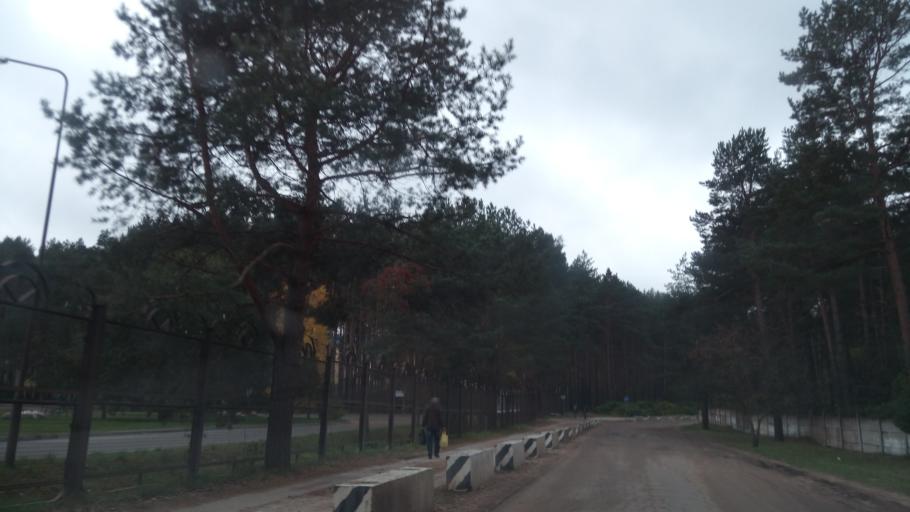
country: BY
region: Minsk
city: Zhdanovichy
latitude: 53.9569
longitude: 27.4414
